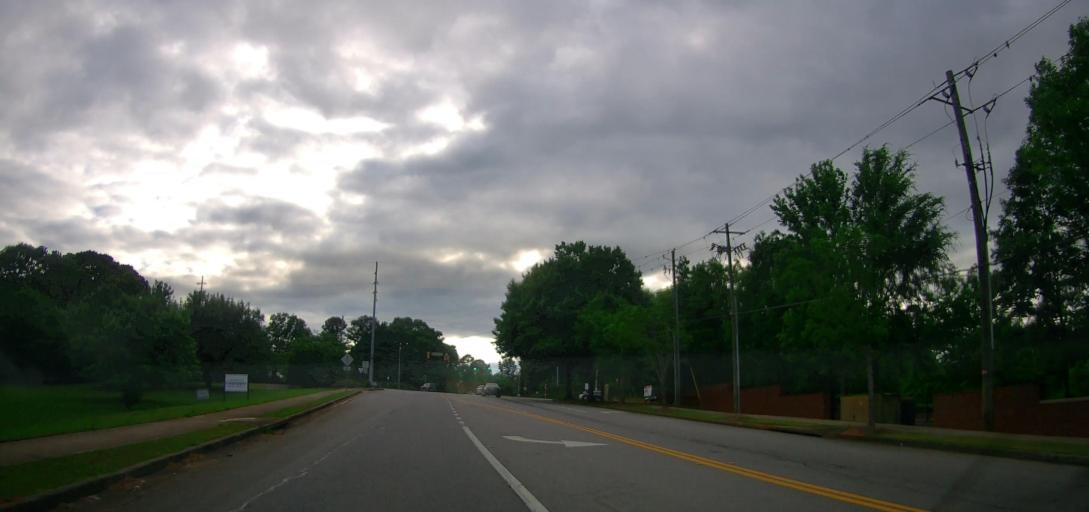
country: US
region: Georgia
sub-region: Clarke County
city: Country Club Estates
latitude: 33.9337
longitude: -83.4361
